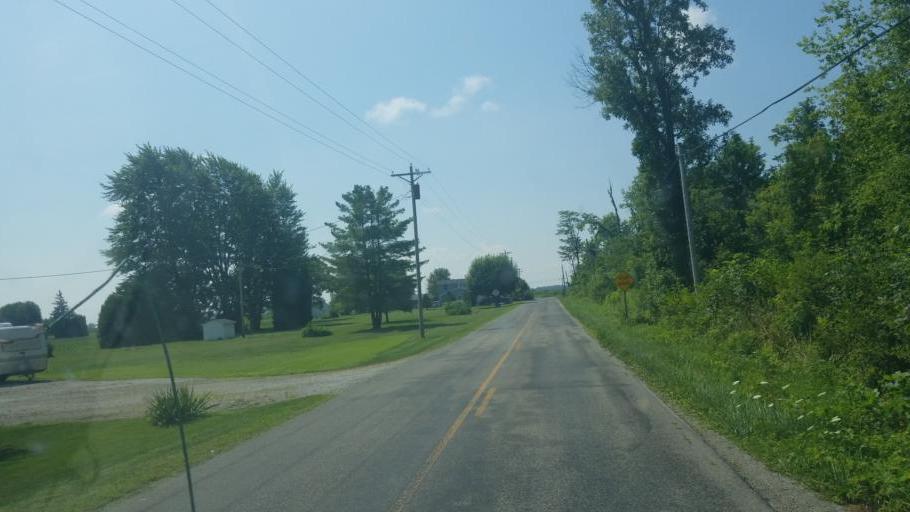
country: US
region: Ohio
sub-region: Hardin County
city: Ada
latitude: 40.6763
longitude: -83.7412
